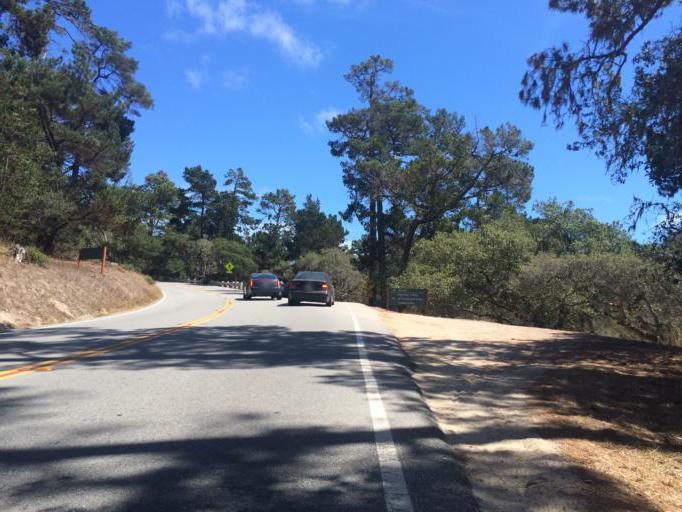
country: US
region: California
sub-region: Monterey County
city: Carmel-by-the-Sea
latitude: 36.5607
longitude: -121.9274
